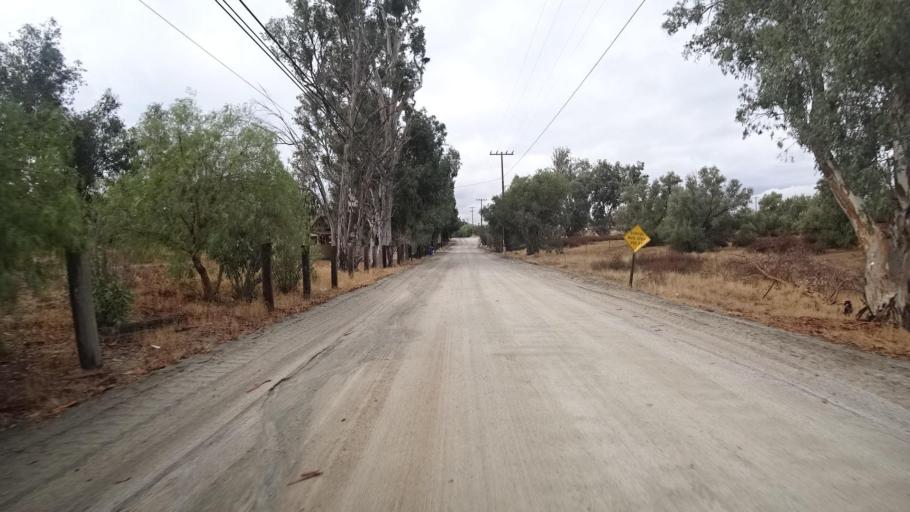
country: MX
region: Baja California
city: Tecate
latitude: 32.5840
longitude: -116.6213
